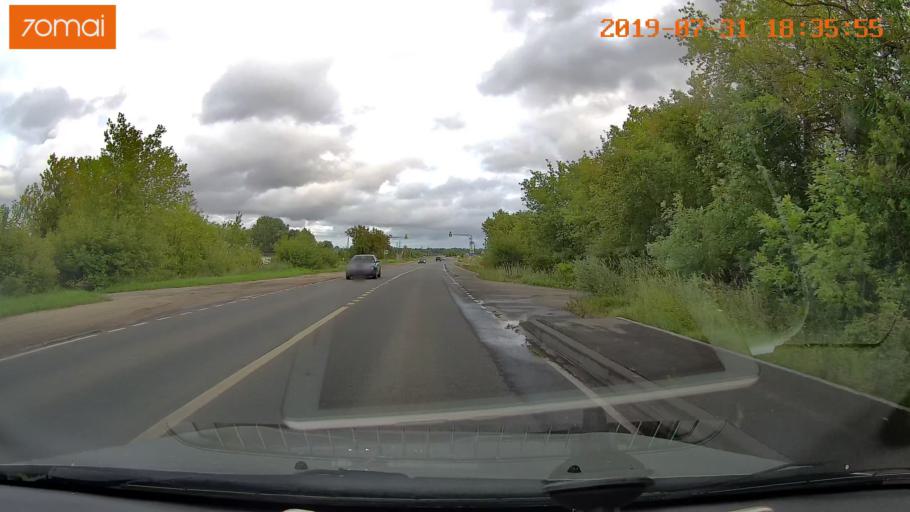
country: RU
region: Moskovskaya
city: Voskresensk
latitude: 55.2918
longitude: 38.6743
